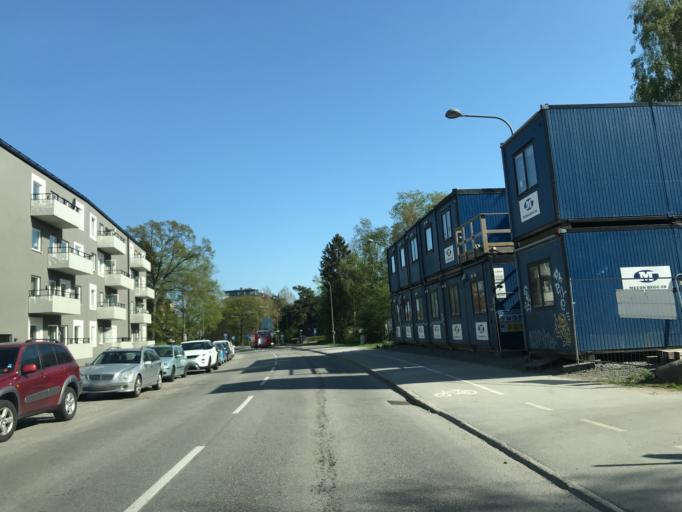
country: SE
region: Stockholm
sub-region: Stockholms Kommun
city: Arsta
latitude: 59.2885
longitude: 18.0046
